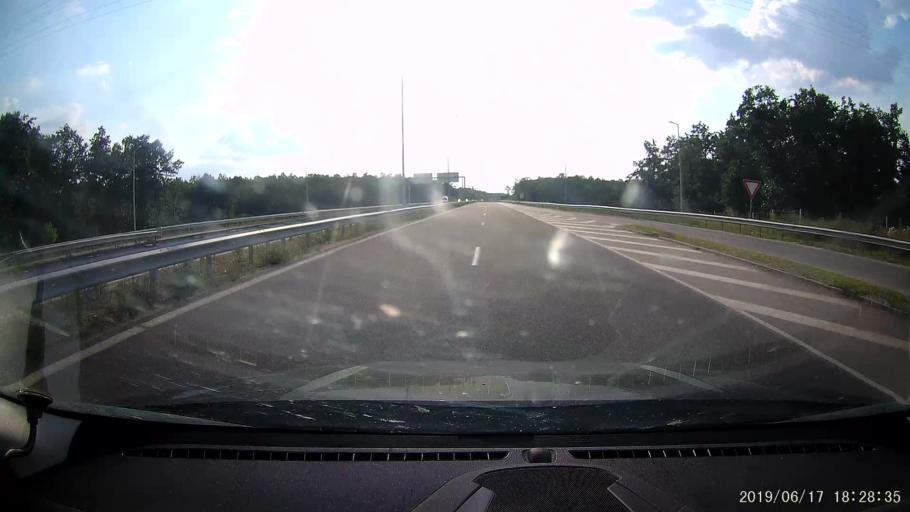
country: BG
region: Khaskovo
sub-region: Obshtina Dimitrovgrad
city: Dimitrovgrad
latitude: 42.0235
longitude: 25.5754
